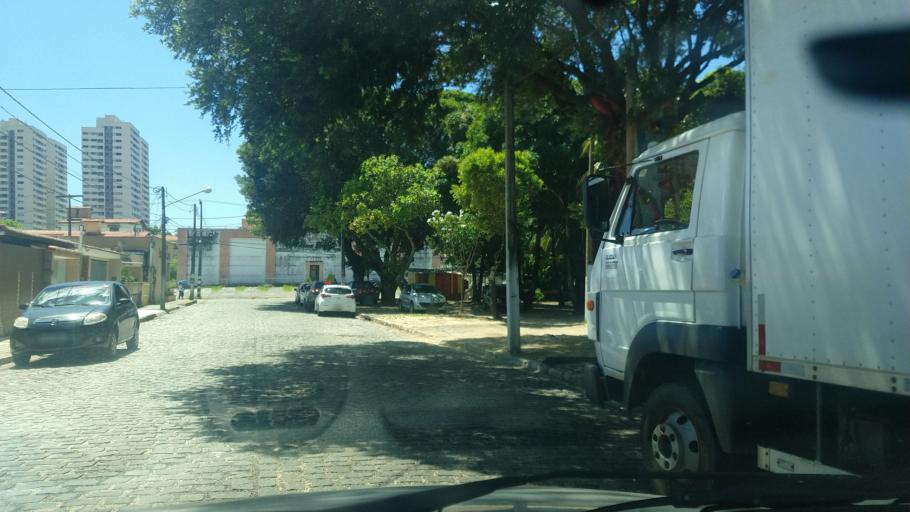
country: BR
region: Rio Grande do Norte
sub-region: Natal
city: Natal
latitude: -5.8555
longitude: -35.2081
